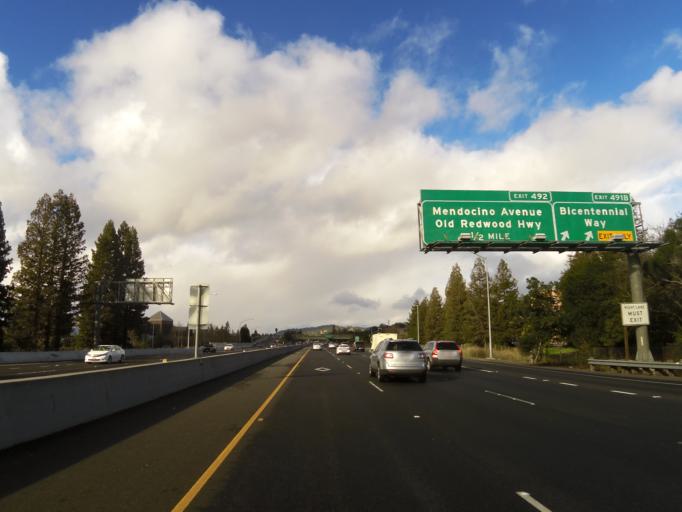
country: US
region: California
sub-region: Sonoma County
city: Santa Rosa
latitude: 38.4664
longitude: -122.7276
